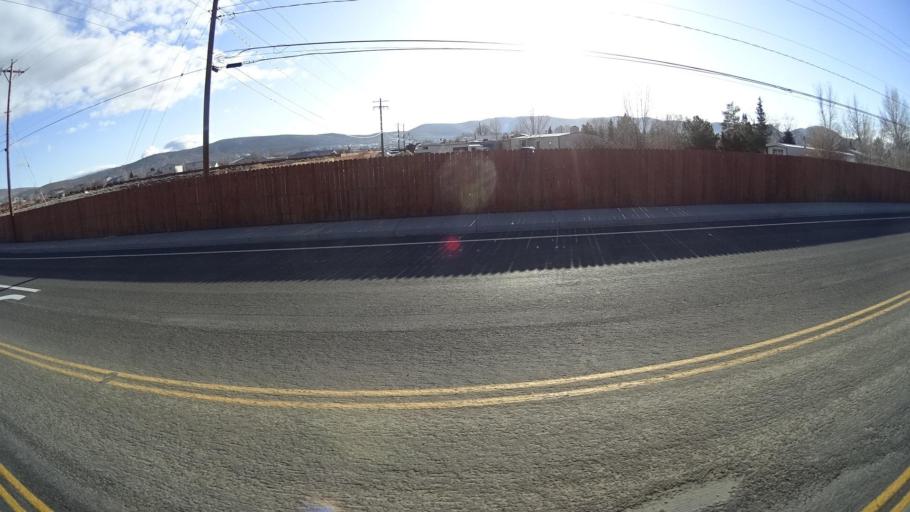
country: US
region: Nevada
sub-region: Washoe County
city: Cold Springs
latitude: 39.6863
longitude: -119.9787
